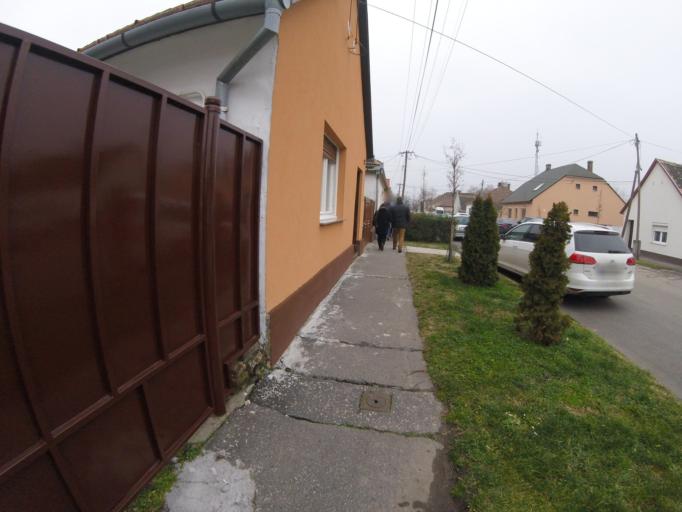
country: HU
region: Baranya
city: Mohacs
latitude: 45.9922
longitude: 18.6848
